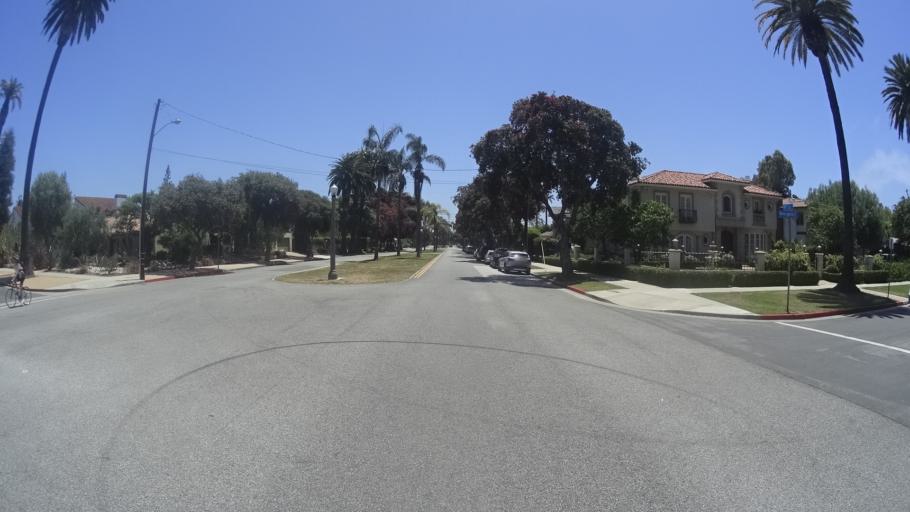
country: US
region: California
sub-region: Los Angeles County
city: Santa Monica
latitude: 34.0283
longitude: -118.5096
